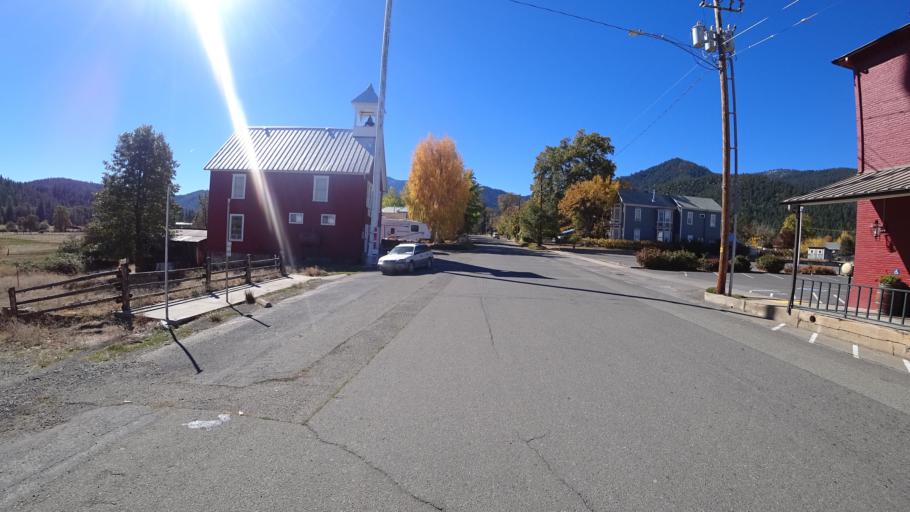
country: US
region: California
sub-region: Siskiyou County
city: Yreka
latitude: 41.4560
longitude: -122.8944
